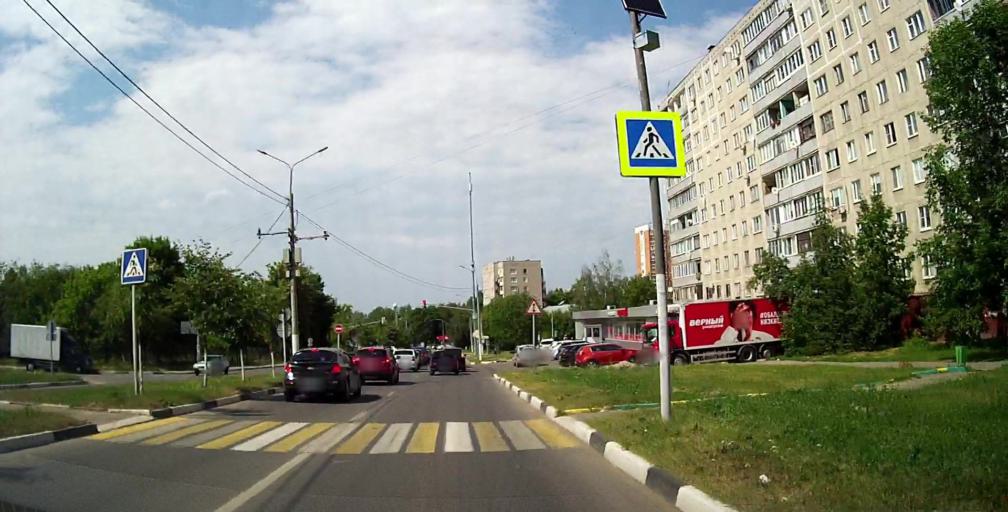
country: RU
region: Moskovskaya
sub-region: Podol'skiy Rayon
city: Podol'sk
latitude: 55.4175
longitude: 37.5203
